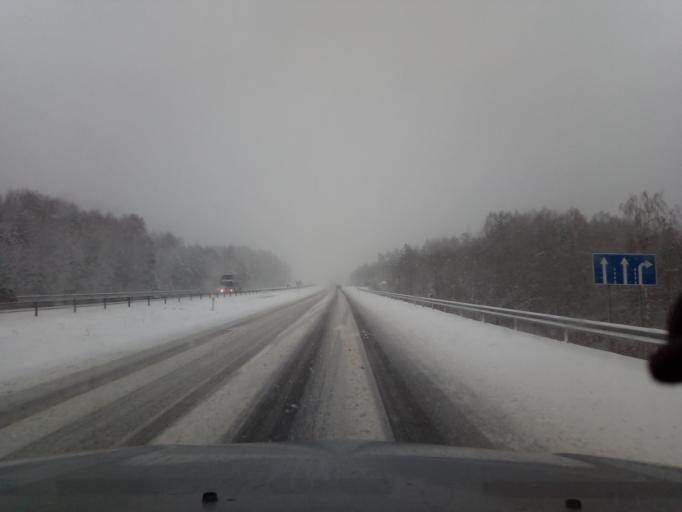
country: LT
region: Vilnius County
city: Pasilaiciai
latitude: 54.7980
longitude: 25.1652
